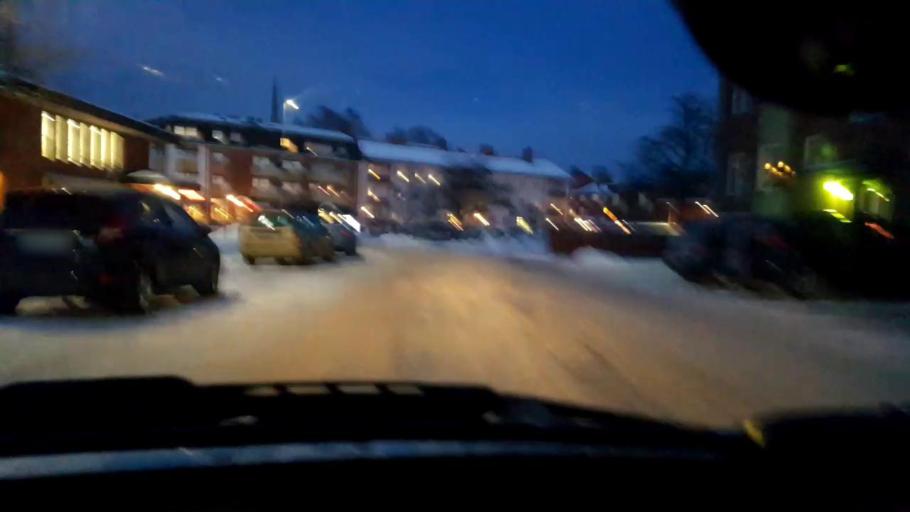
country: SE
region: Dalarna
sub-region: Mora Kommun
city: Mora
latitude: 61.0052
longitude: 14.5362
